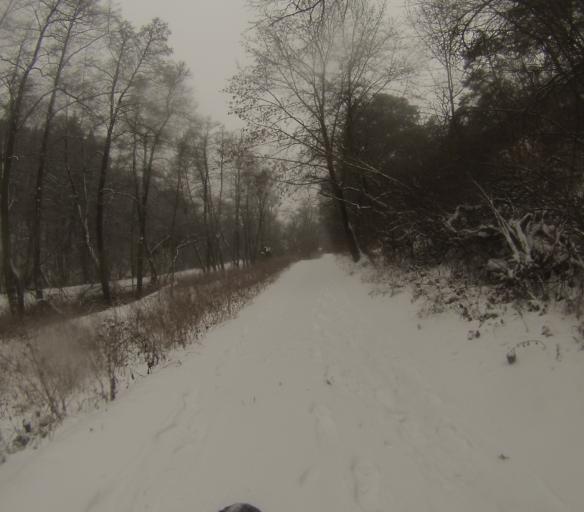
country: CZ
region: South Moravian
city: Ostopovice
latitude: 49.1299
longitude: 16.5502
